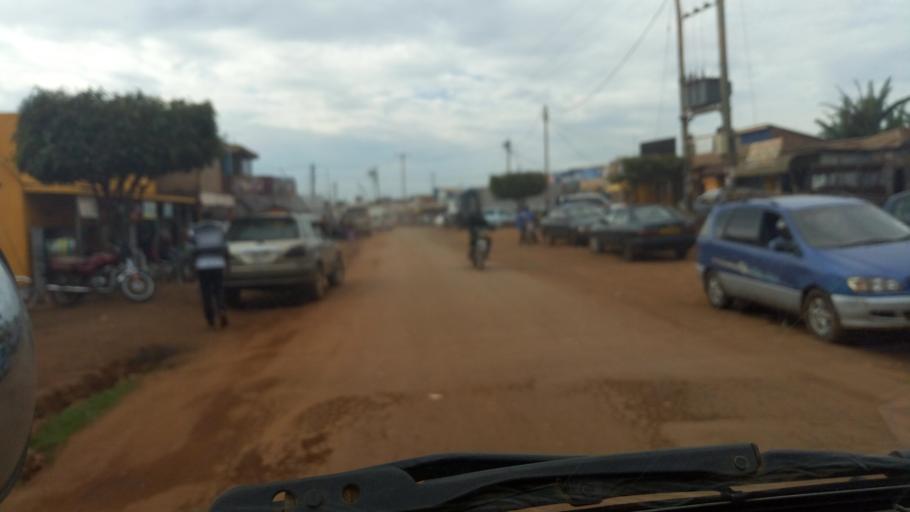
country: UG
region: Central Region
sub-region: Mukono District
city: Mukono
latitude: 0.3677
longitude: 32.7138
